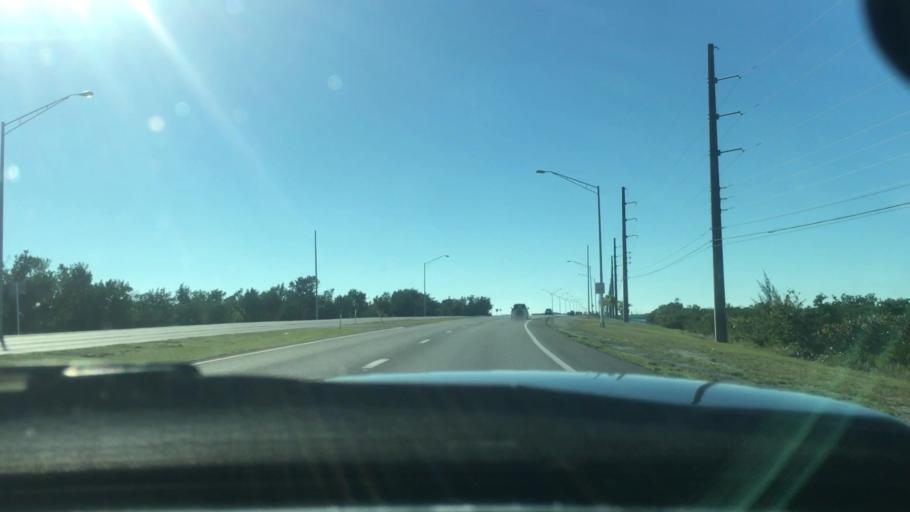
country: US
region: Florida
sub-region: Monroe County
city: Stock Island
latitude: 24.5788
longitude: -81.7099
